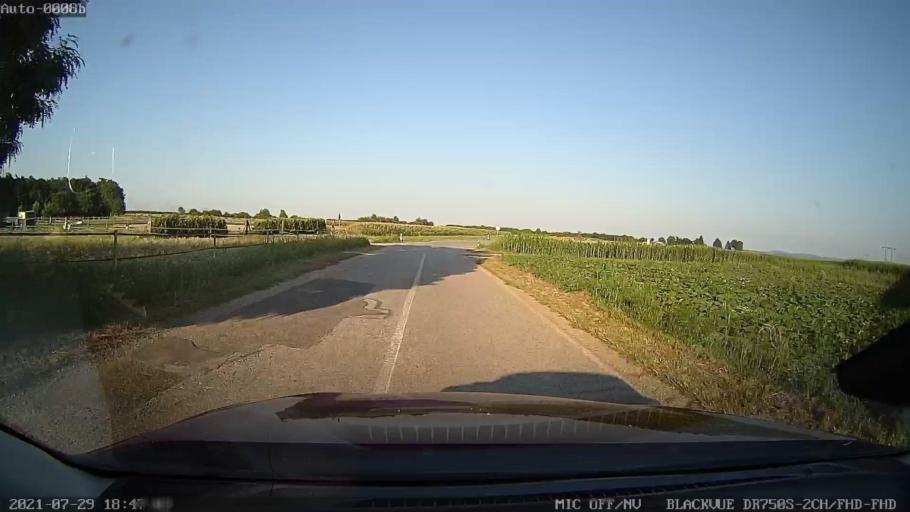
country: HR
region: Varazdinska
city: Sracinec
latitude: 46.3133
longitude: 16.2716
